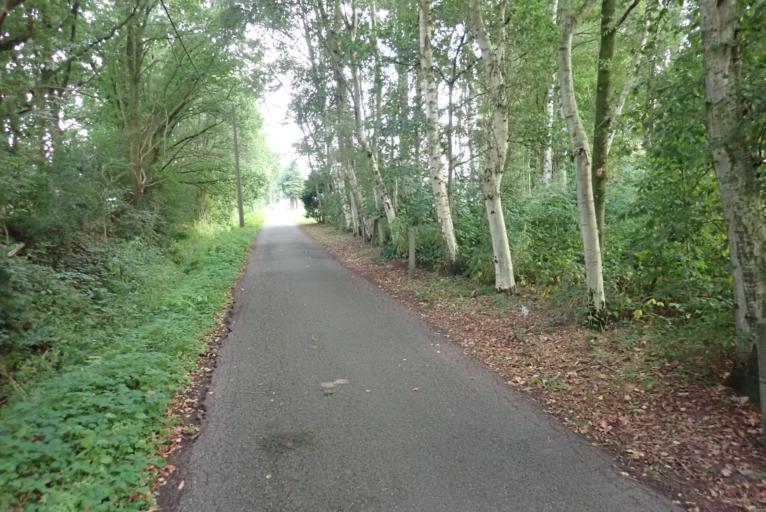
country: BE
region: Flanders
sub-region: Provincie Antwerpen
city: Essen
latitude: 51.4718
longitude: 4.5005
